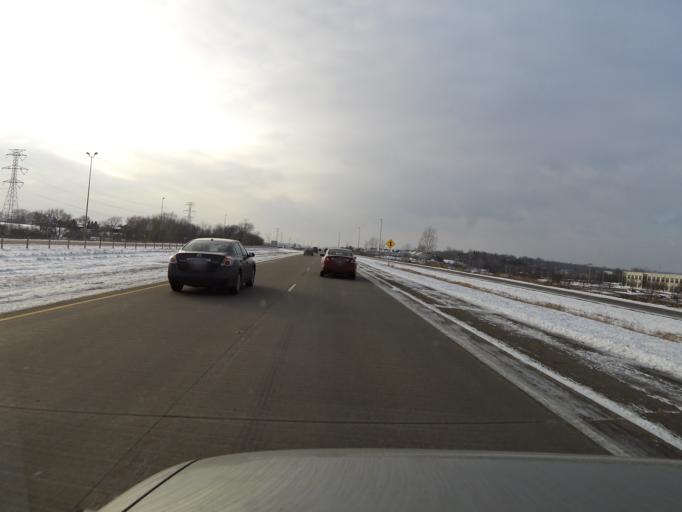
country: US
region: Minnesota
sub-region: Scott County
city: Shakopee
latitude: 44.7818
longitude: -93.4726
